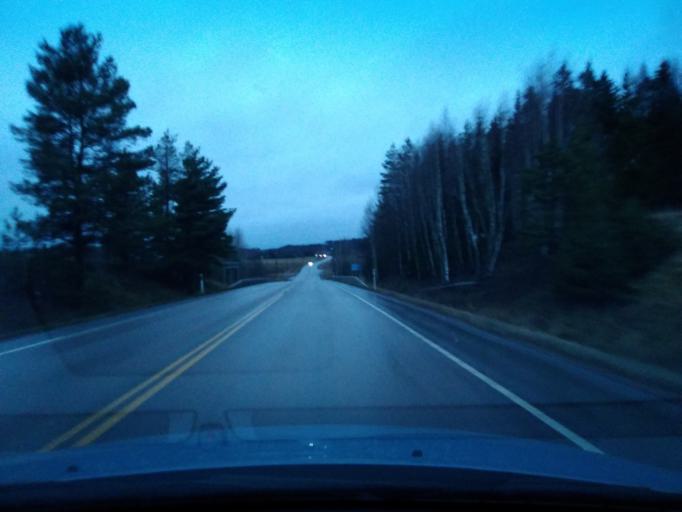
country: FI
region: Uusimaa
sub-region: Porvoo
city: Askola
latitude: 60.4508
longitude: 25.5845
